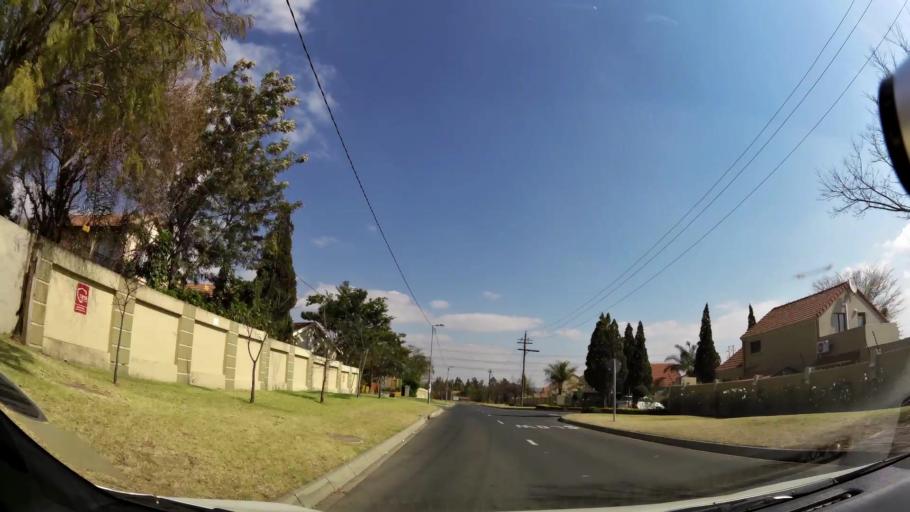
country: ZA
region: Gauteng
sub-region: City of Johannesburg Metropolitan Municipality
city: Midrand
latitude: -26.0128
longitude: 28.0727
